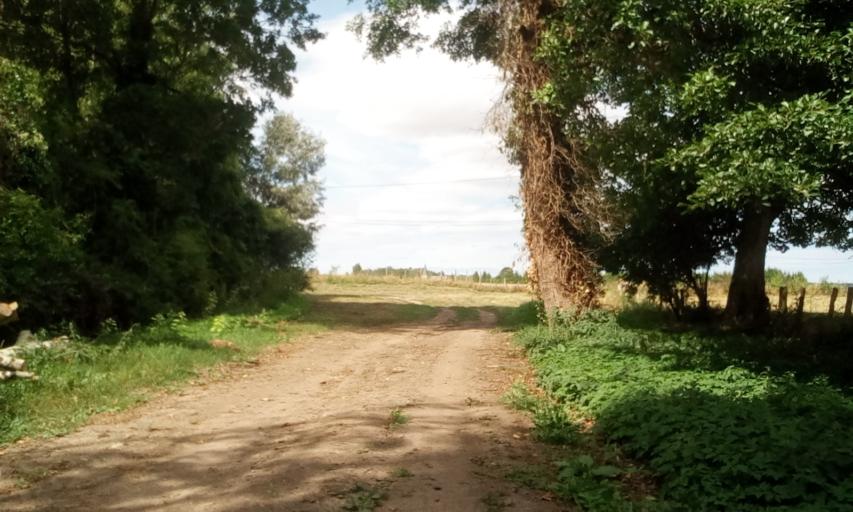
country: FR
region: Lower Normandy
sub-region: Departement du Calvados
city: Sannerville
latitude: 49.1616
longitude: -0.2151
